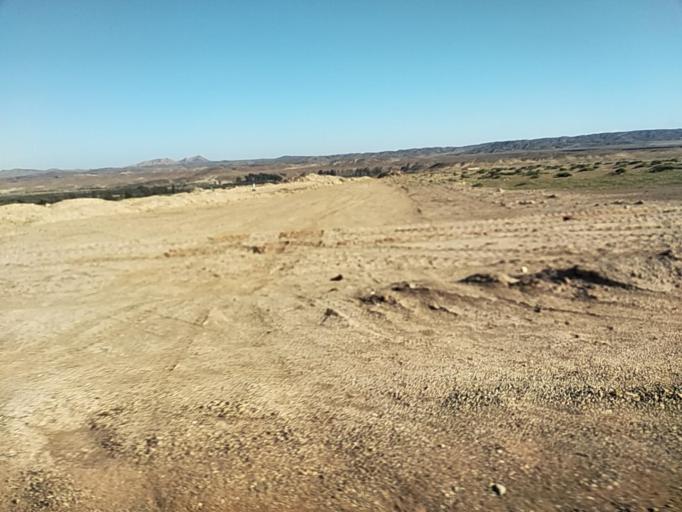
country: CL
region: Atacama
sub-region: Provincia de Copiapo
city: Copiapo
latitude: -27.3306
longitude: -70.7841
